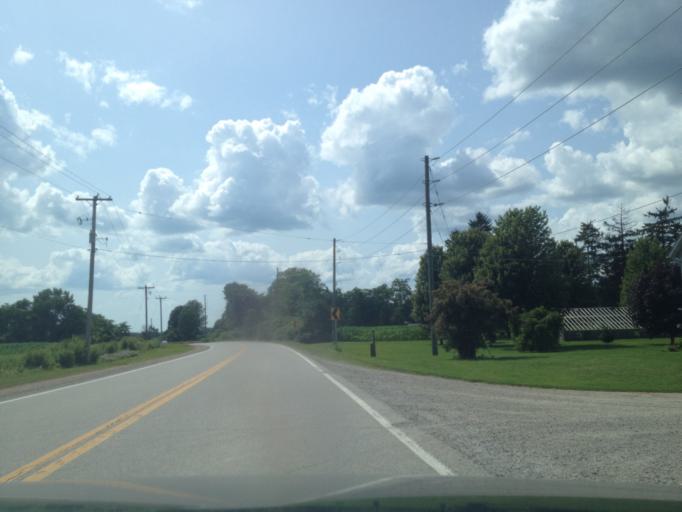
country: CA
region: Ontario
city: Aylmer
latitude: 42.6742
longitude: -80.8964
